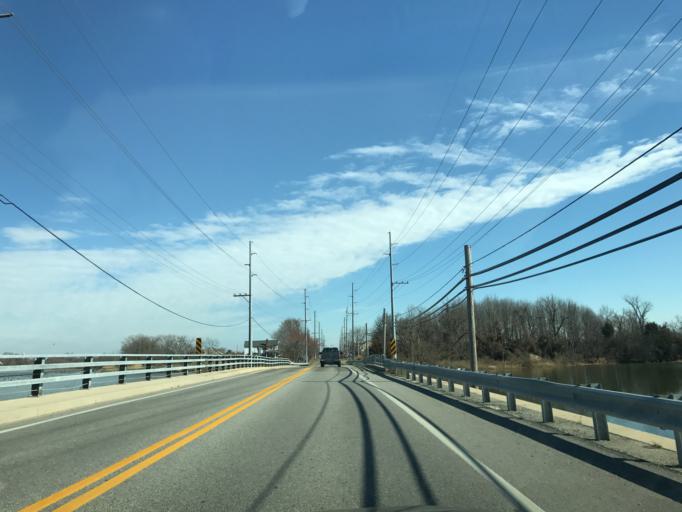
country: US
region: Maryland
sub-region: Queen Anne's County
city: Stevensville
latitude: 38.9770
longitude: -76.3039
